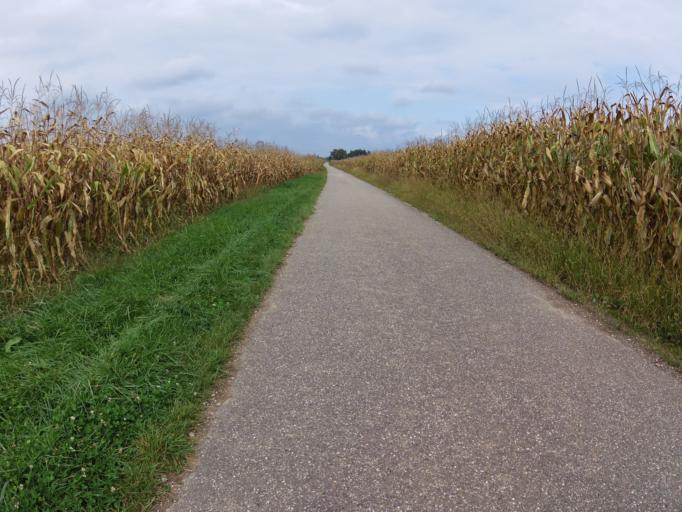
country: FR
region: Alsace
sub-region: Departement du Haut-Rhin
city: Biesheim
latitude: 48.0279
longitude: 7.5389
